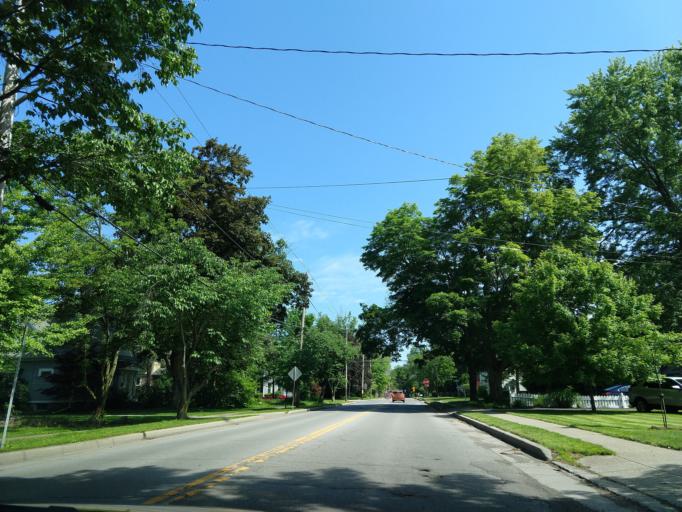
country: US
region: New York
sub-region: Erie County
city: East Aurora
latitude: 42.7650
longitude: -78.6224
